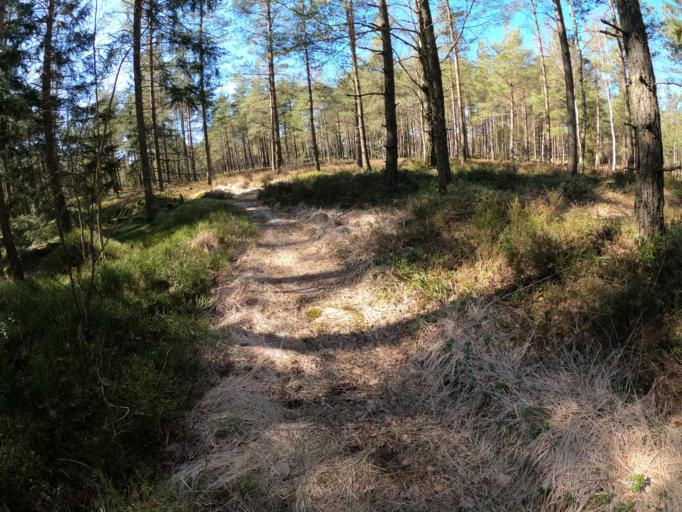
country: SE
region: Vaestra Goetaland
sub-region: Harryda Kommun
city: Molnlycke
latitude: 57.6229
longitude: 12.1232
